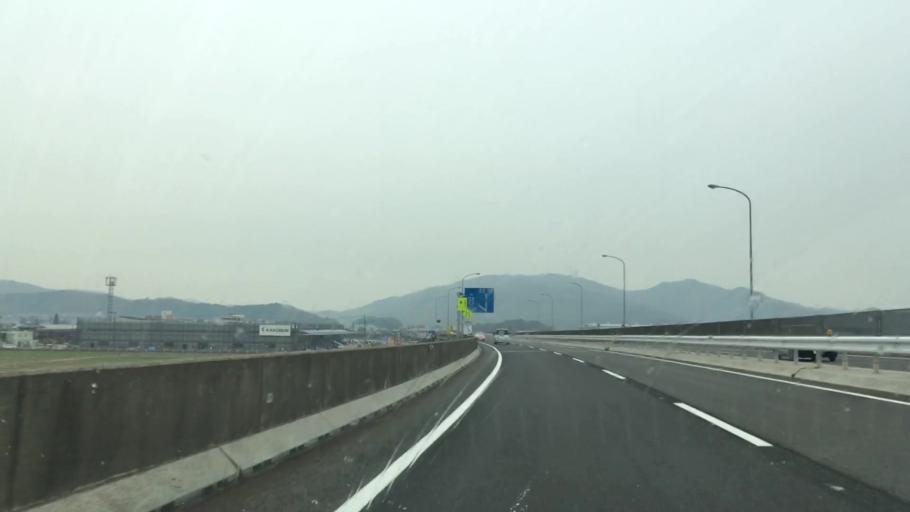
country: JP
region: Aichi
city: Nishio
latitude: 34.8700
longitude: 137.0854
